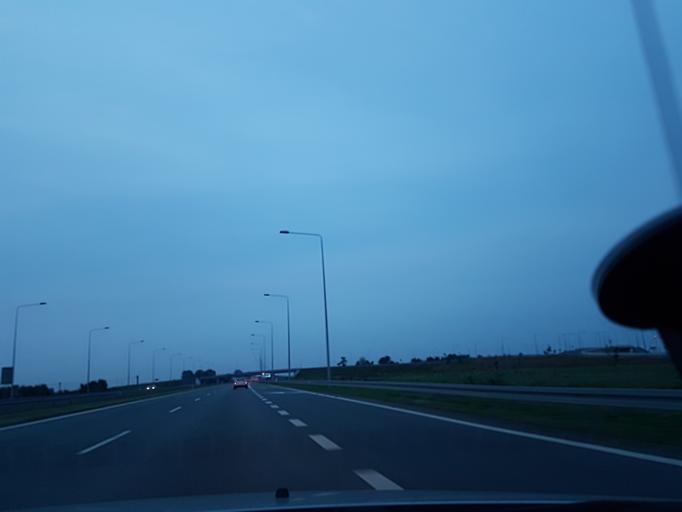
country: PL
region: Lodz Voivodeship
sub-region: Powiat kutnowski
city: Krzyzanow
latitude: 52.2225
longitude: 19.4682
